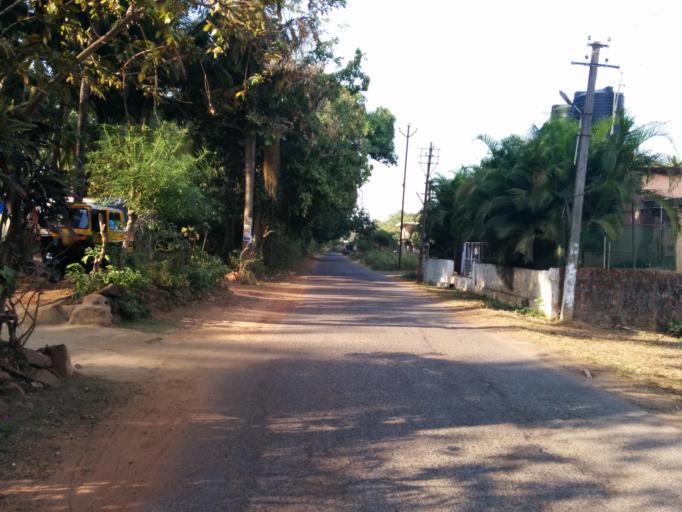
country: IN
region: Karnataka
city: Canacona
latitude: 15.0076
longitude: 74.0300
